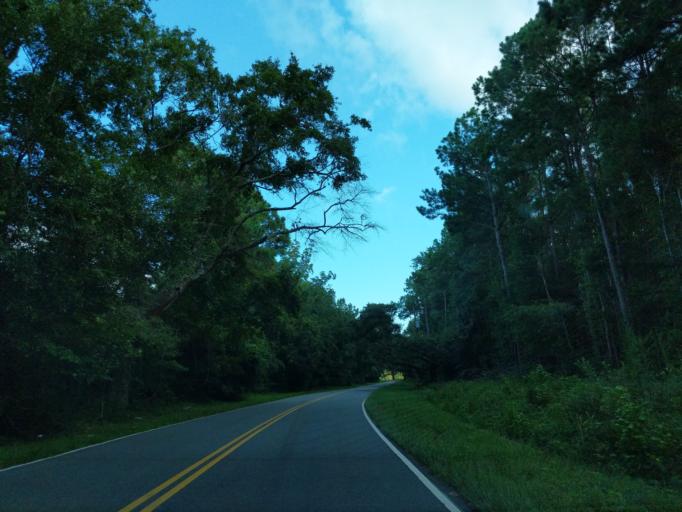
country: US
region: South Carolina
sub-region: Charleston County
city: Awendaw
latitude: 33.0959
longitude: -79.4660
